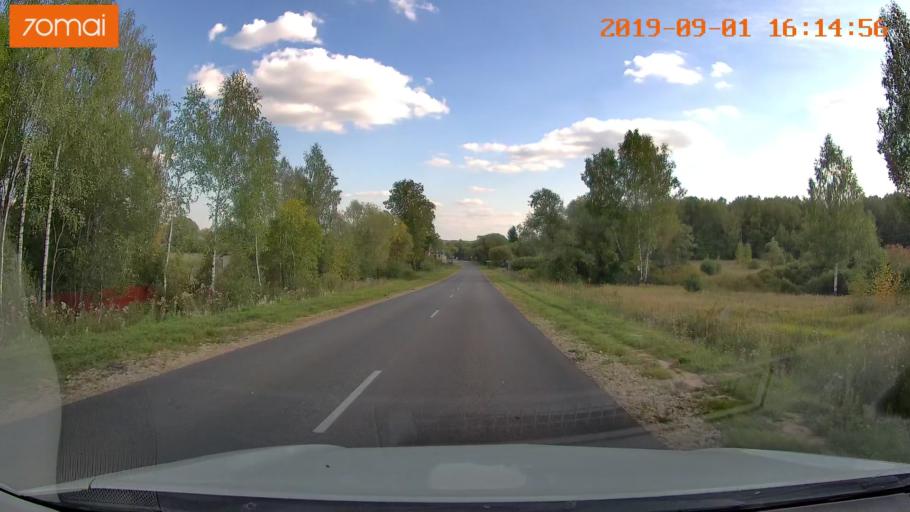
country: RU
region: Kaluga
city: Maloyaroslavets
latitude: 54.9270
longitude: 36.4733
